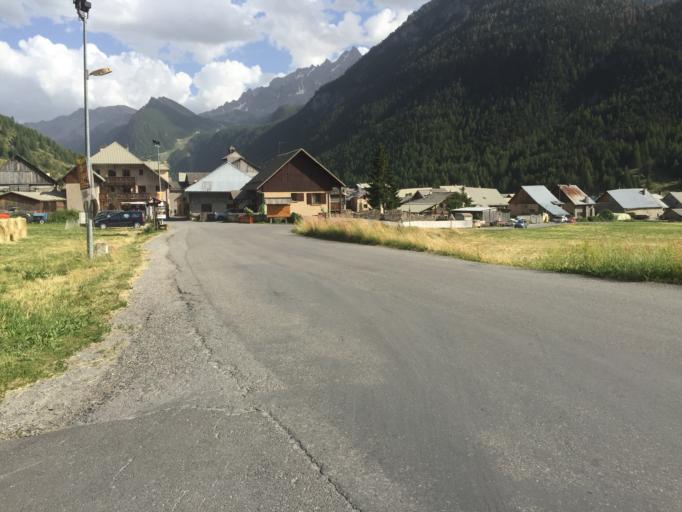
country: FR
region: Provence-Alpes-Cote d'Azur
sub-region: Departement des Hautes-Alpes
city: Guillestre
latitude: 44.6698
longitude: 6.7771
